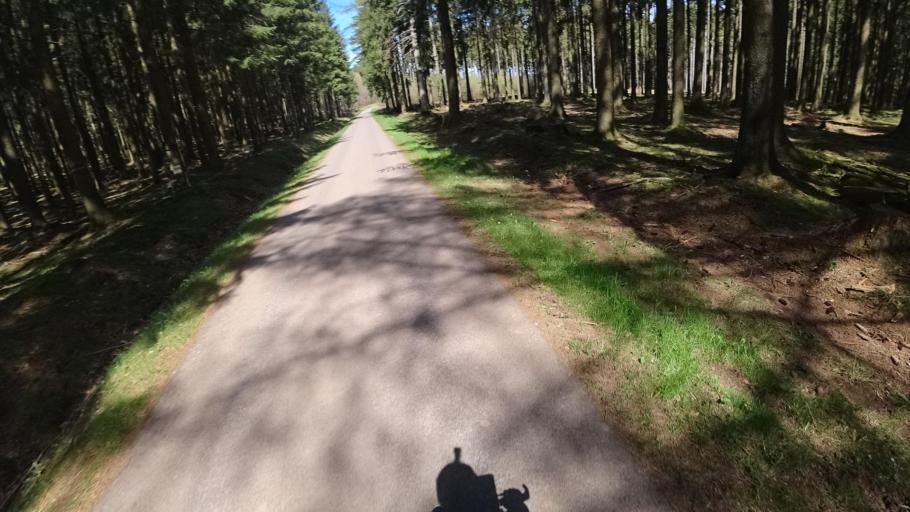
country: DE
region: Rheinland-Pfalz
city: Gusenburg
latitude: 49.6339
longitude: 6.8857
